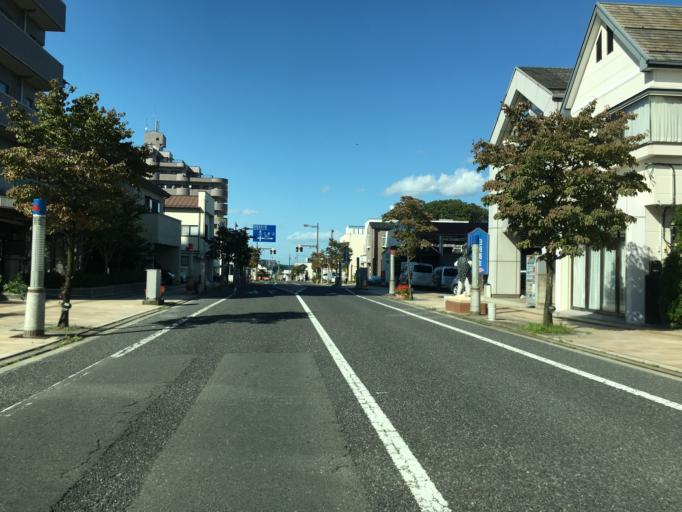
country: JP
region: Fukushima
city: Sukagawa
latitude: 37.2922
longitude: 140.3760
